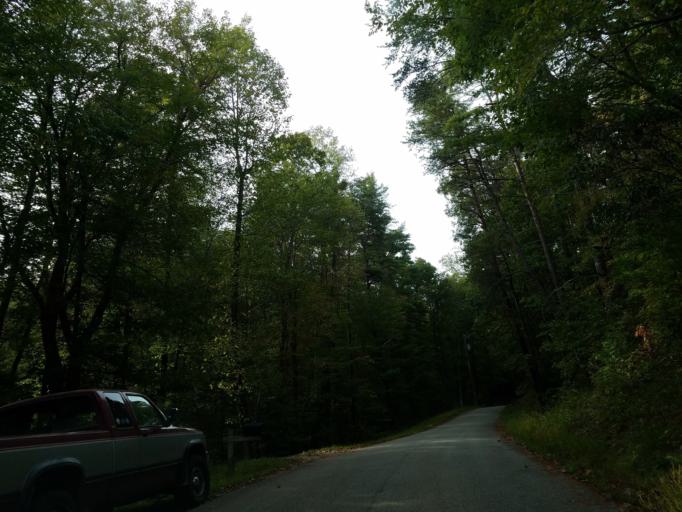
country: US
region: Georgia
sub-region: Dawson County
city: Dawsonville
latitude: 34.5703
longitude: -84.1707
